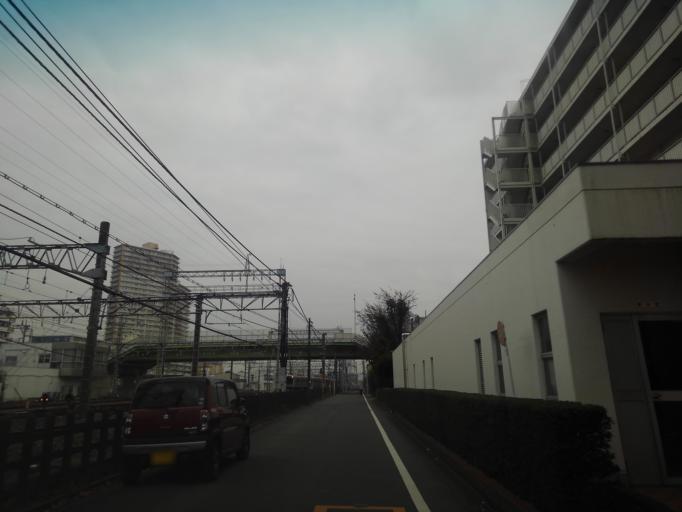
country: JP
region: Saitama
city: Tokorozawa
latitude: 35.8022
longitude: 139.4340
